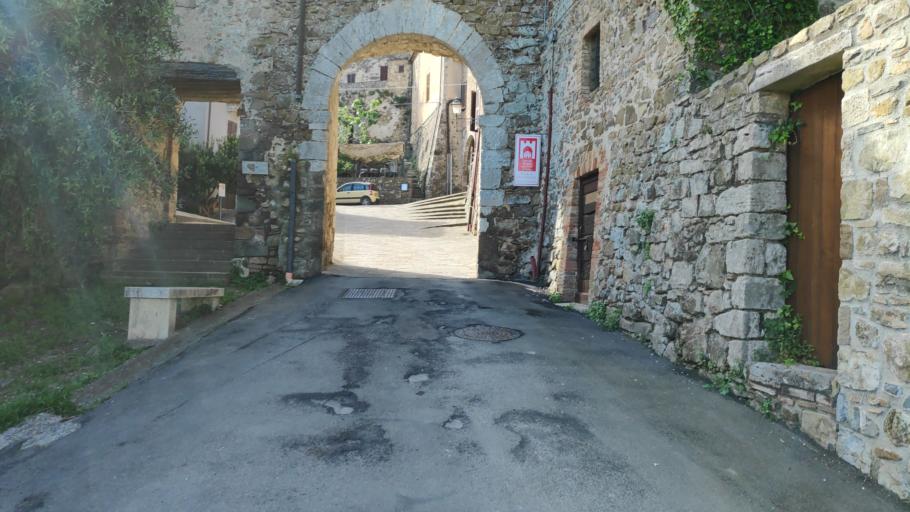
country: IT
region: Tuscany
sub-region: Provincia di Grosseto
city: Manciano
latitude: 42.6224
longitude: 11.4905
